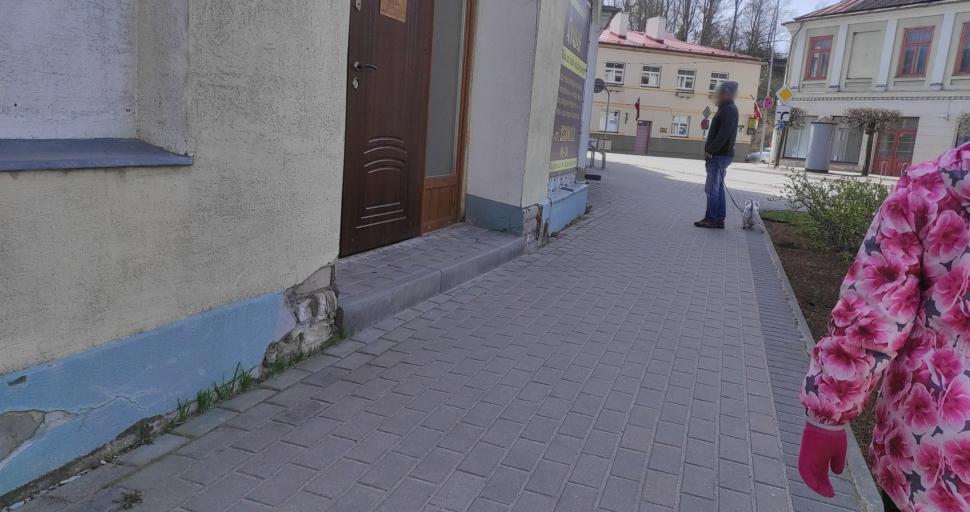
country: LV
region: Talsu Rajons
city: Talsi
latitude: 57.2448
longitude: 22.5924
